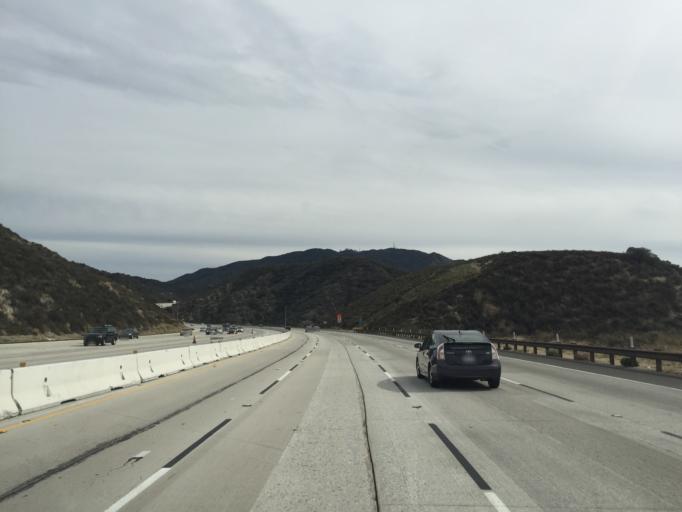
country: US
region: California
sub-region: Los Angeles County
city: Burbank
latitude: 34.2442
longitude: -118.3192
